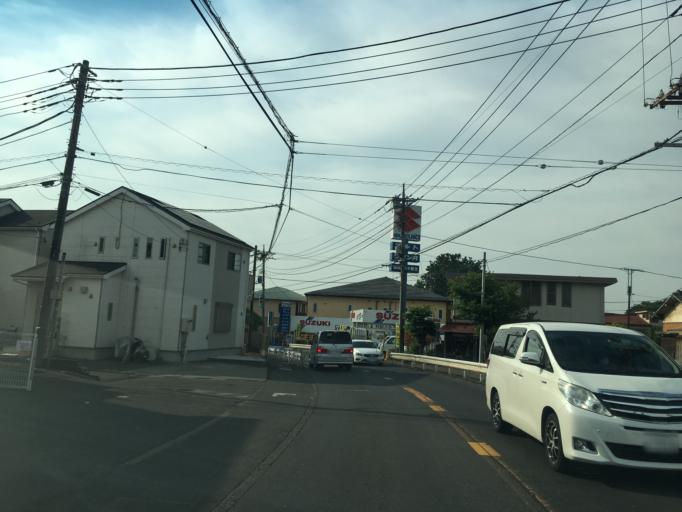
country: JP
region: Saitama
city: Tokorozawa
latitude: 35.7872
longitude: 139.5074
